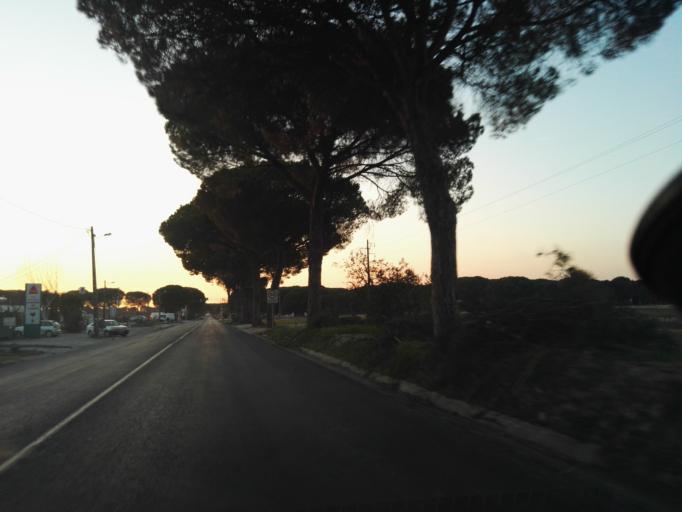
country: PT
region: Santarem
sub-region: Benavente
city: Poceirao
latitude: 38.6874
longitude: -8.7286
